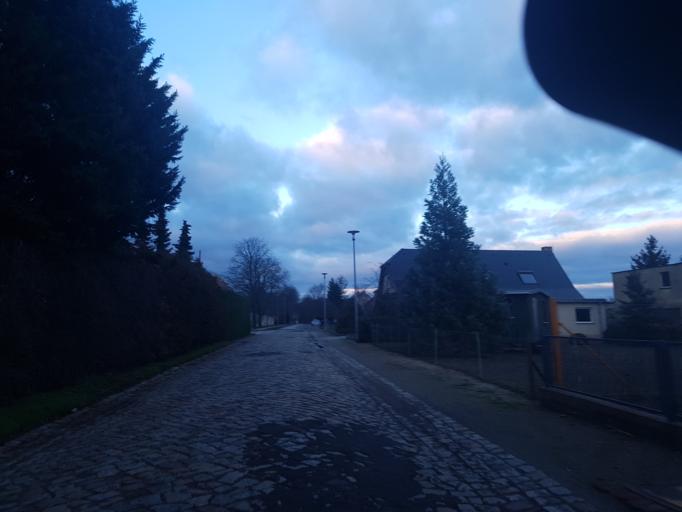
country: DE
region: Brandenburg
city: Muhlberg
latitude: 51.4709
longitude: 13.2036
